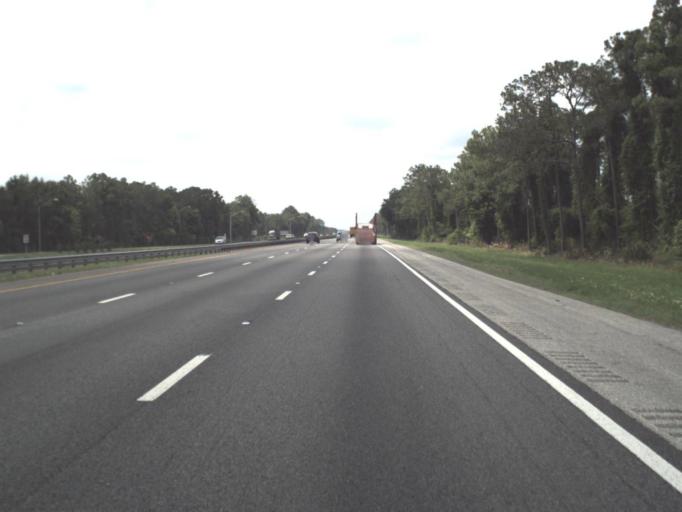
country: US
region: Florida
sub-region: Saint Johns County
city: Saint Augustine Shores
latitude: 29.7157
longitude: -81.3334
